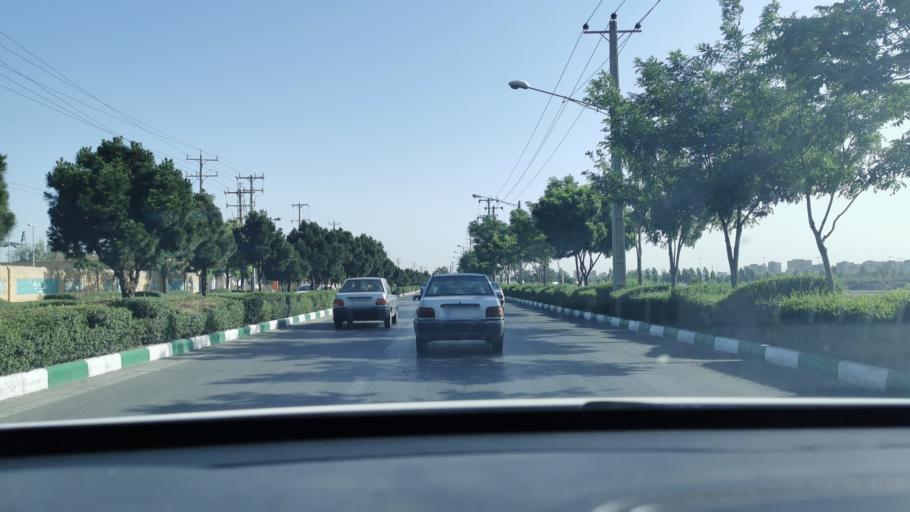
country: IR
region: Razavi Khorasan
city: Mashhad
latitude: 36.3420
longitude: 59.5079
